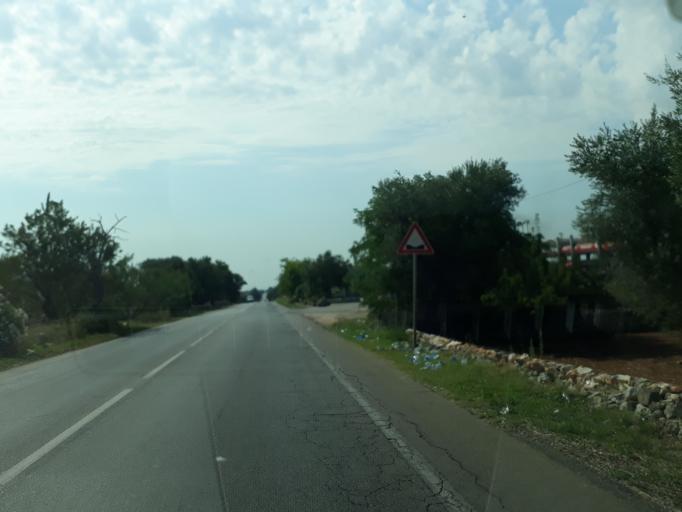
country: IT
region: Apulia
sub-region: Provincia di Brindisi
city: Carovigno
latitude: 40.6879
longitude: 17.6765
